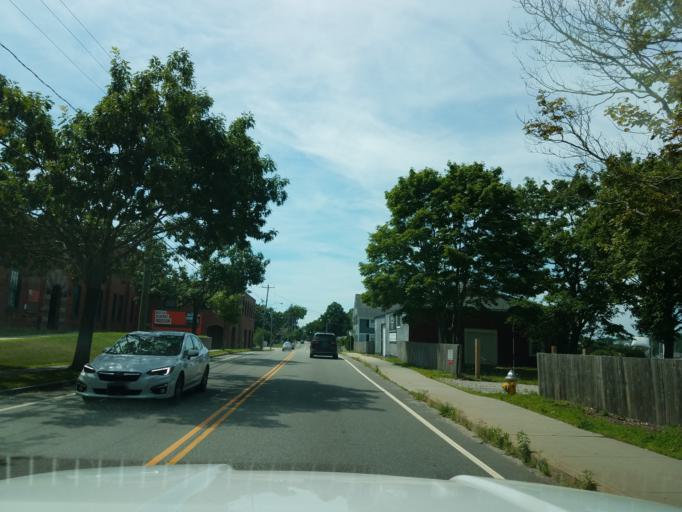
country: US
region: Connecticut
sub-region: New London County
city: Mystic
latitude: 41.3649
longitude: -71.9628
